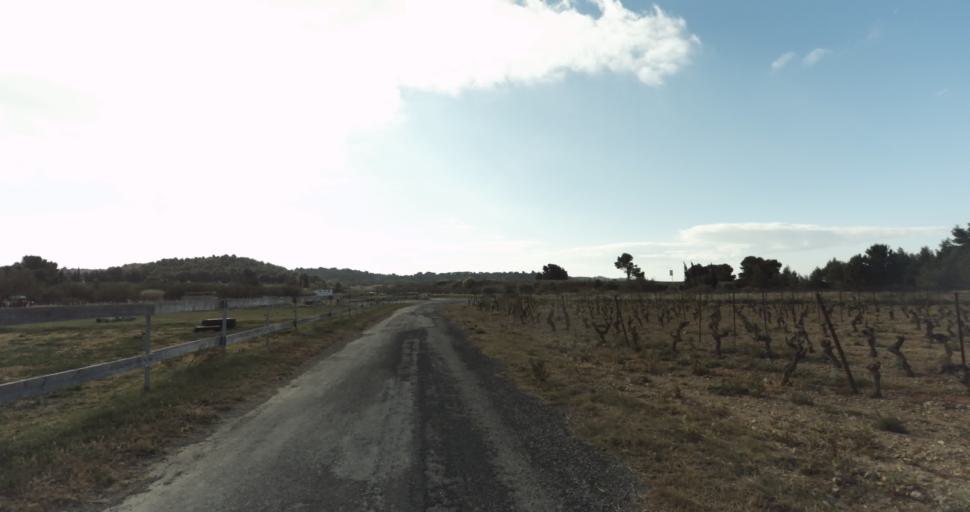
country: FR
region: Languedoc-Roussillon
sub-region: Departement de l'Aude
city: Leucate
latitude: 42.9304
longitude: 3.0073
